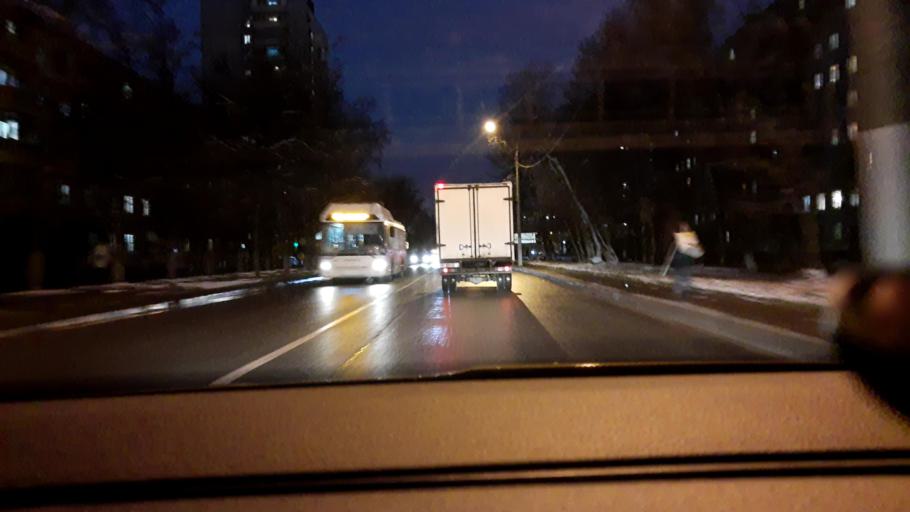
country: RU
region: Moskovskaya
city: Dolgoprudnyy
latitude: 55.9453
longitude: 37.4917
